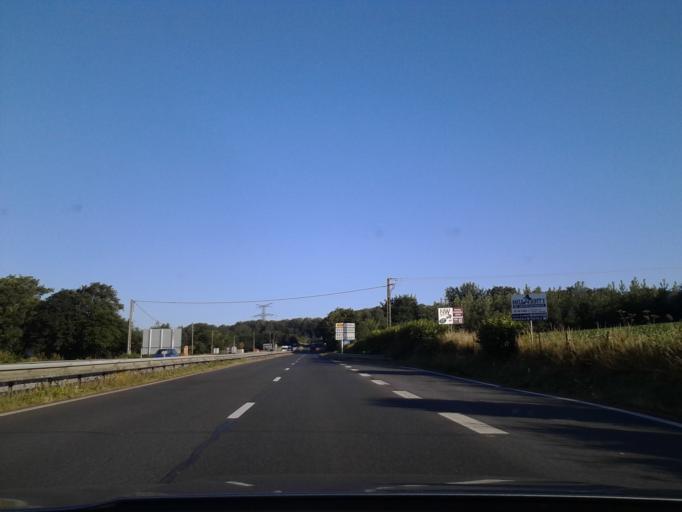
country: FR
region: Lower Normandy
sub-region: Departement de la Manche
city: Brix
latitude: 49.5444
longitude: -1.5533
